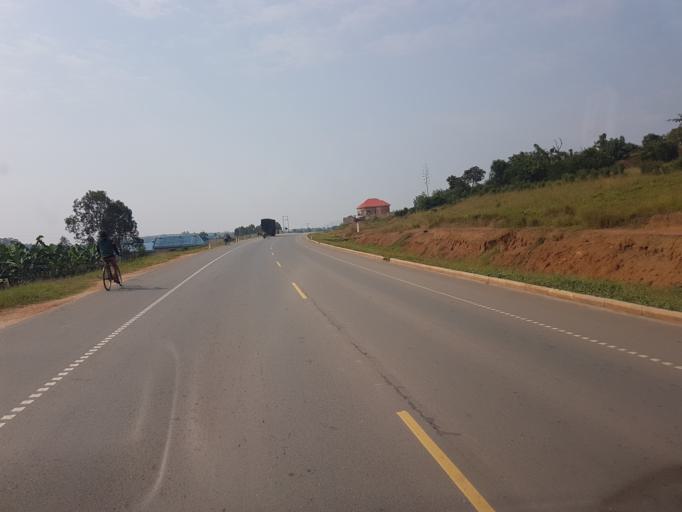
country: UG
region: Western Region
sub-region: Mbarara District
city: Bwizibwera
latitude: -0.6340
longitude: 30.6011
